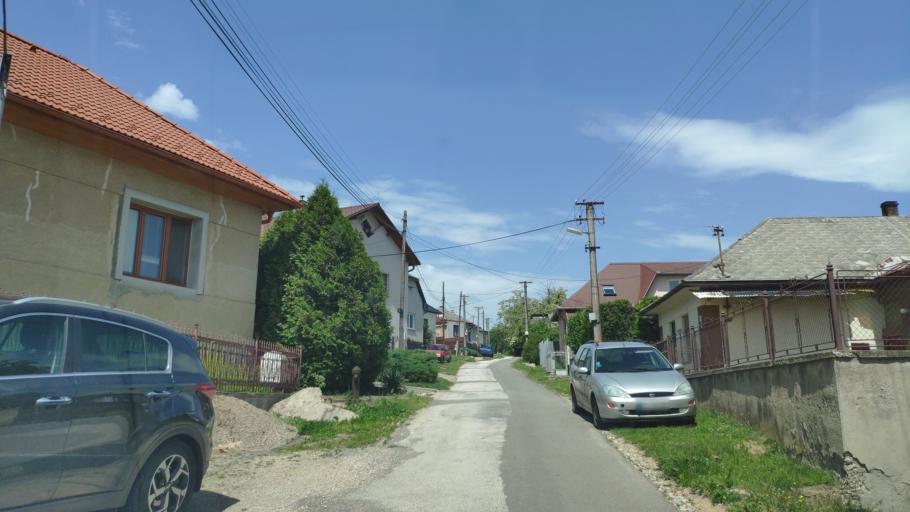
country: SK
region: Kosicky
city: Medzev
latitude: 48.7153
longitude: 20.9735
